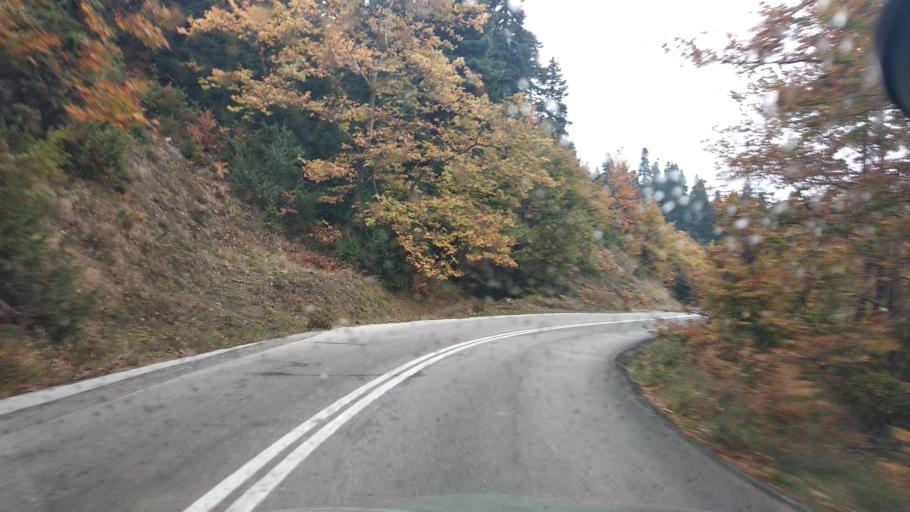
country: GR
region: Thessaly
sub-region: Trikala
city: Pyli
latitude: 39.5174
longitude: 21.5254
